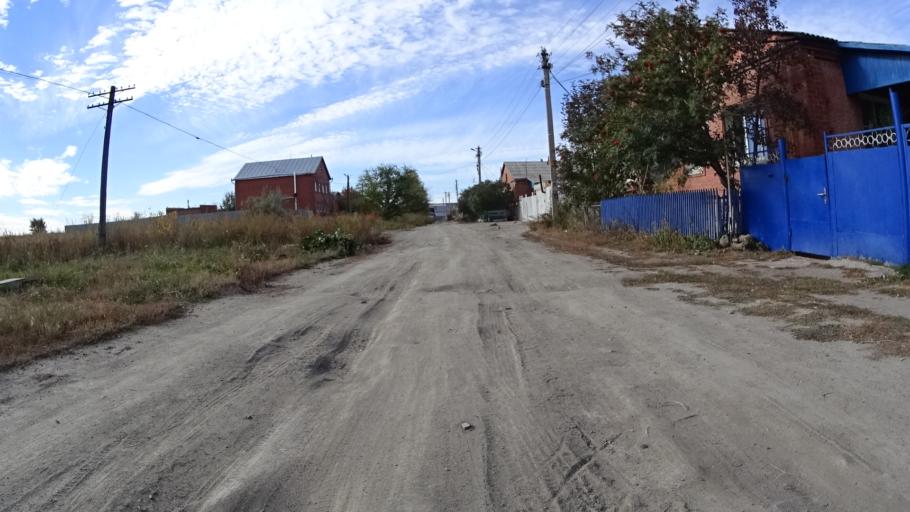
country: RU
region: Chelyabinsk
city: Troitsk
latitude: 54.0743
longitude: 61.5899
